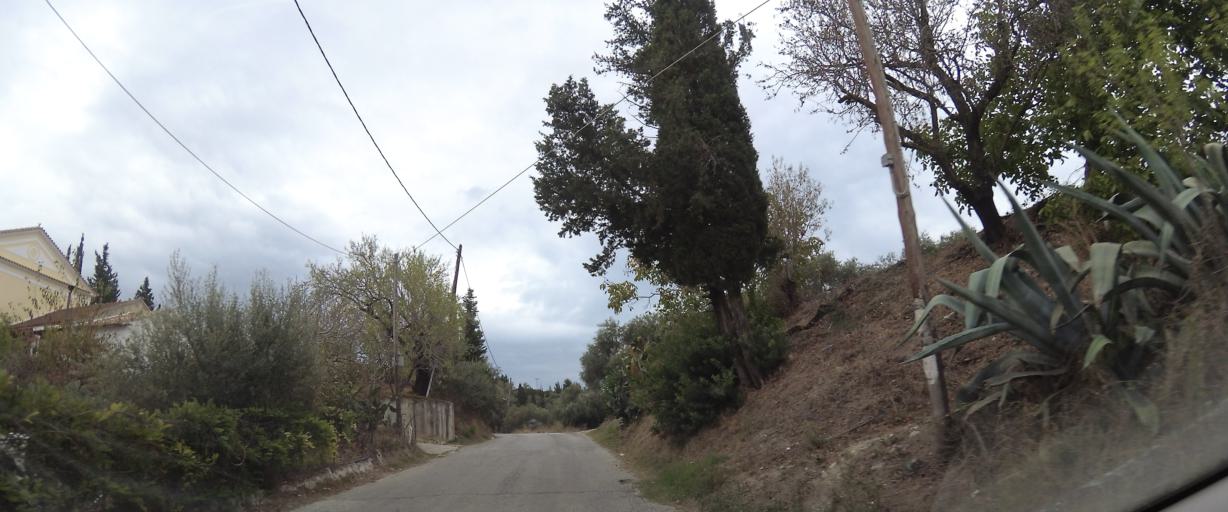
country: GR
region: Ionian Islands
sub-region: Nomos Kerkyras
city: Agios Georgis
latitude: 39.7435
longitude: 19.6785
